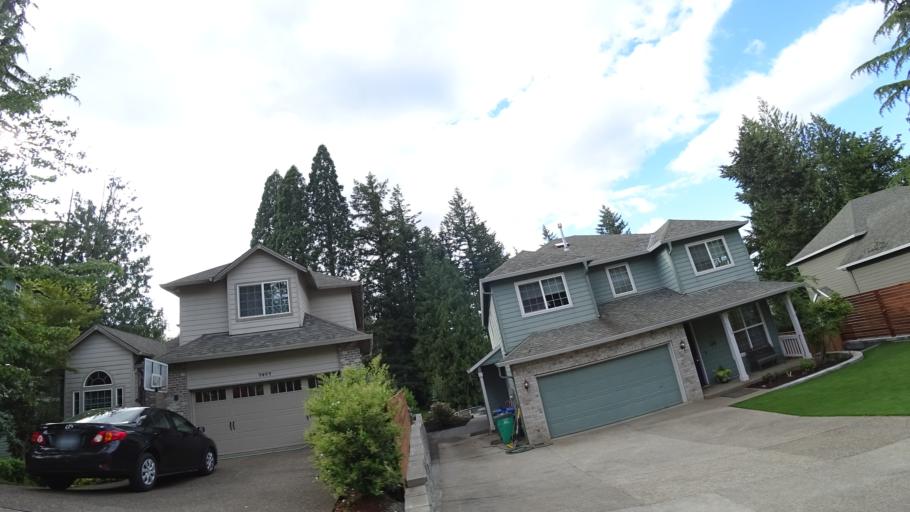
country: US
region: Oregon
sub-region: Washington County
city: Garden Home-Whitford
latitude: 45.4710
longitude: -122.7274
